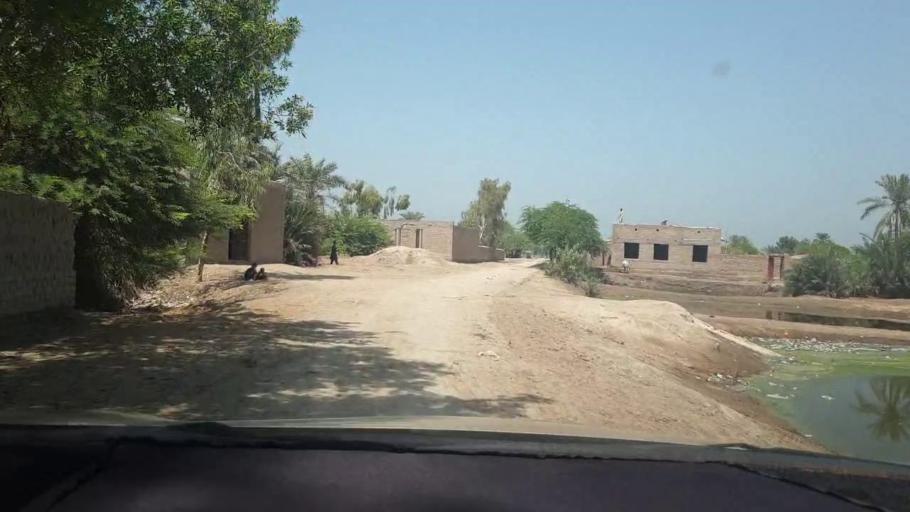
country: PK
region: Sindh
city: Kambar
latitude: 27.6251
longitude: 68.0516
